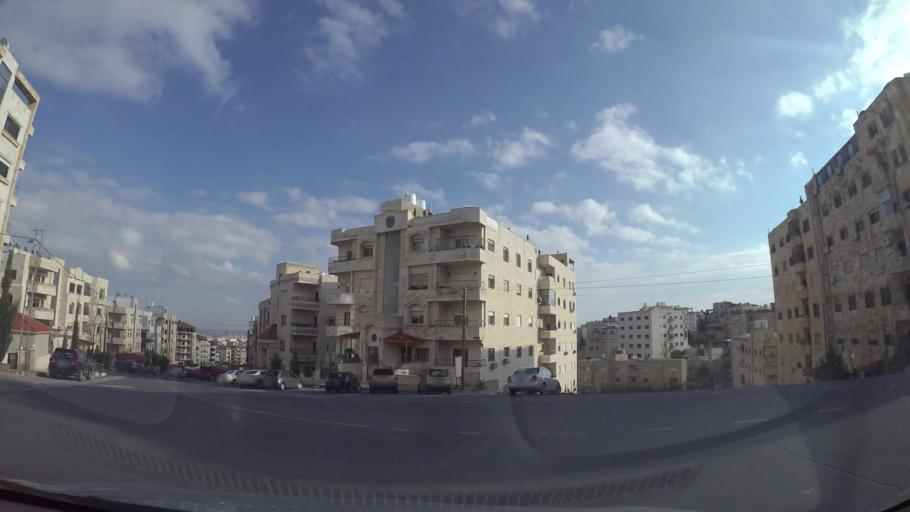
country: JO
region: Amman
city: Al Jubayhah
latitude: 32.0058
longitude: 35.8601
